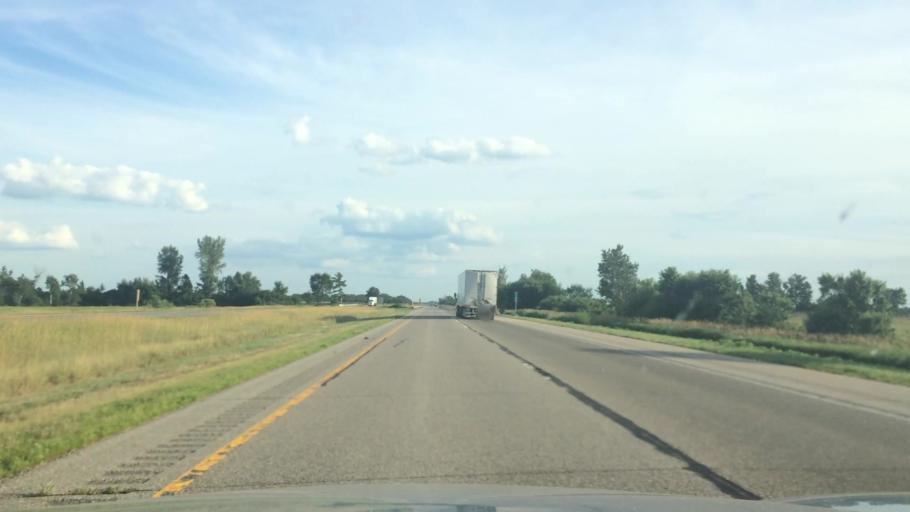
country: US
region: Wisconsin
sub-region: Portage County
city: Plover
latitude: 44.3915
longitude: -89.5198
